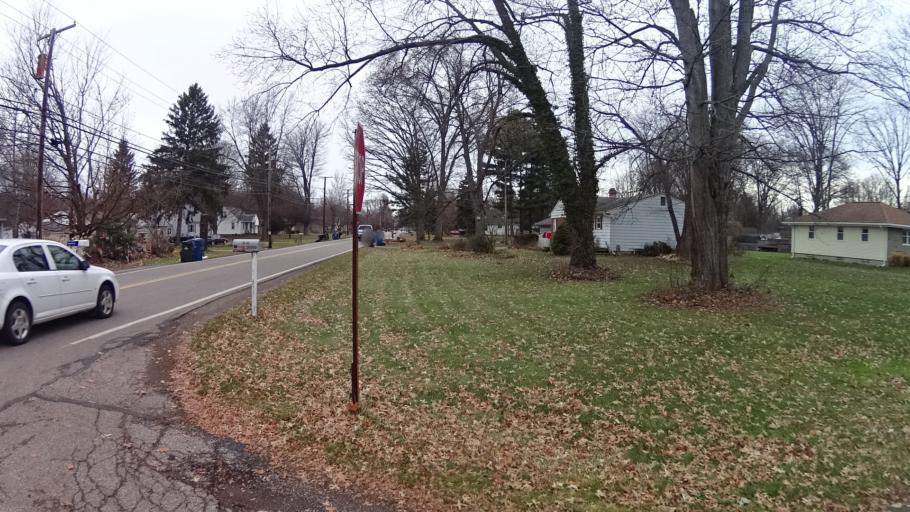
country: US
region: Ohio
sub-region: Lorain County
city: North Ridgeville
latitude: 41.3576
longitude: -82.0265
